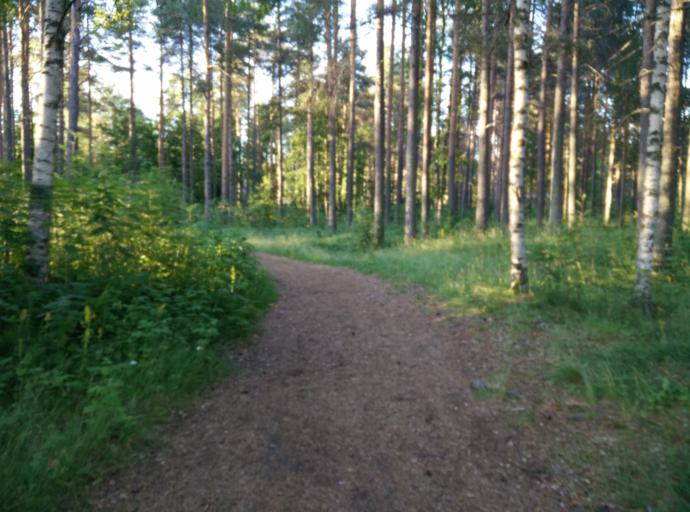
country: FI
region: Lapland
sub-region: Rovaniemi
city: Rovaniemi
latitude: 66.4795
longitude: 25.7054
